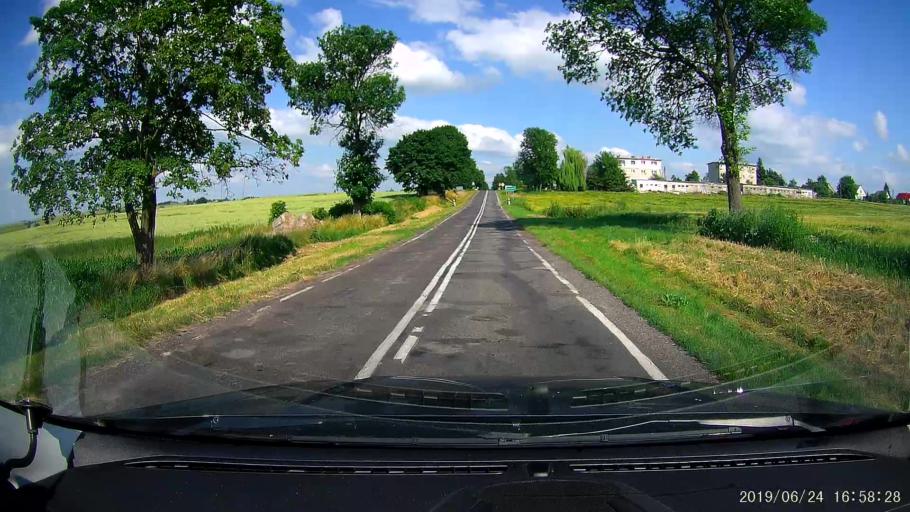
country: PL
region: Lublin Voivodeship
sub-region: Powiat tomaszowski
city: Telatyn
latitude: 50.5251
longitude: 23.8818
